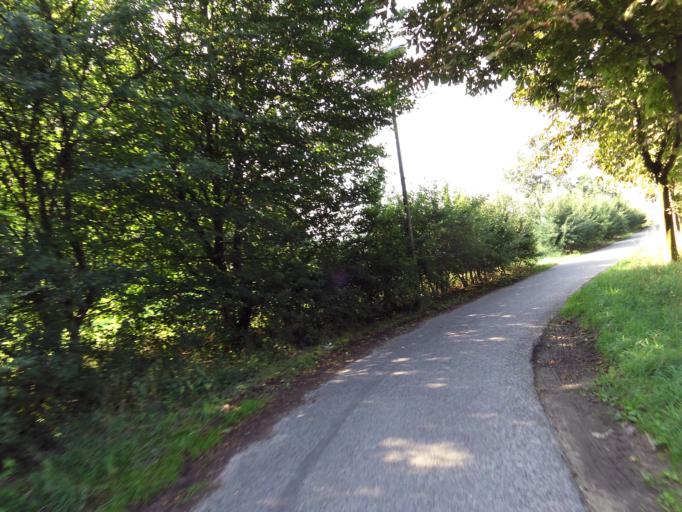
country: DE
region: North Rhine-Westphalia
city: Geilenkirchen
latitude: 50.9687
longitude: 6.1323
